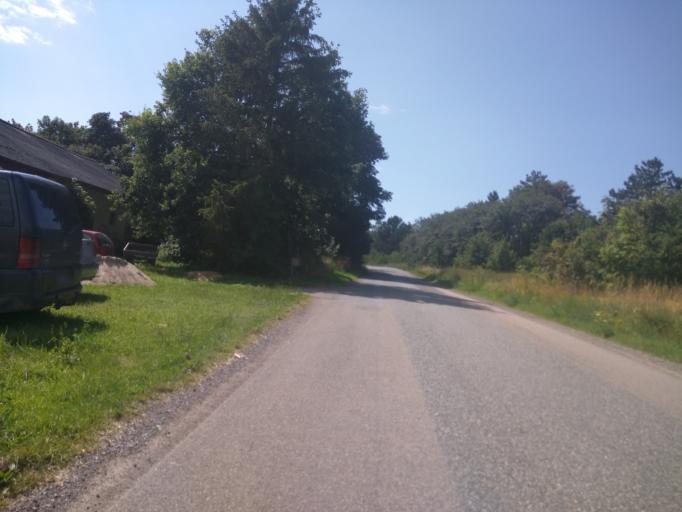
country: DK
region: Zealand
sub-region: Kalundborg Kommune
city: Svebolle
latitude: 55.6902
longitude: 11.2574
